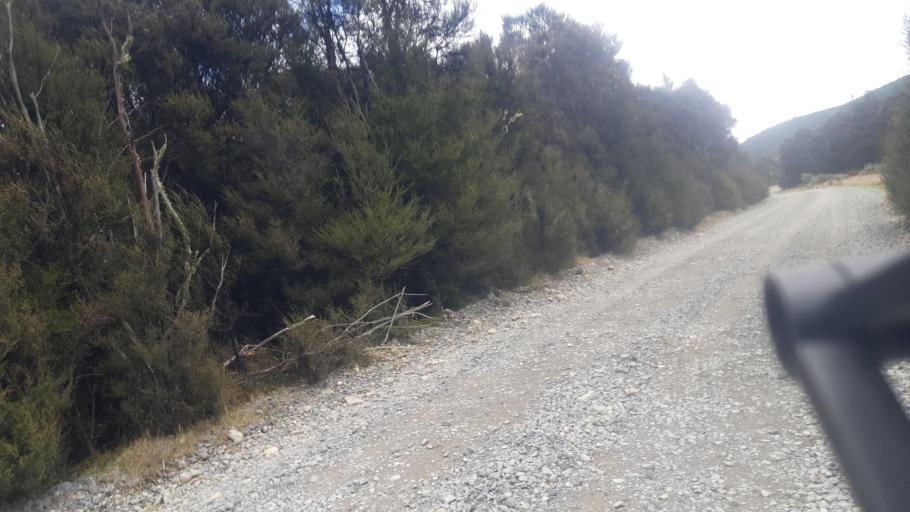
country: NZ
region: Tasman
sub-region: Tasman District
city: Wakefield
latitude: -41.7903
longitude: 172.8267
